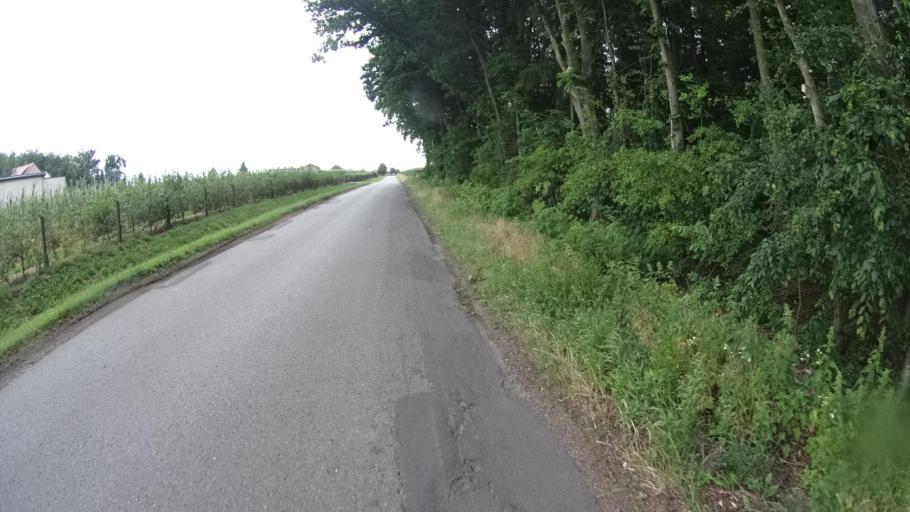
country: PL
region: Masovian Voivodeship
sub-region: Powiat grojecki
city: Goszczyn
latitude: 51.7761
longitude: 20.8536
